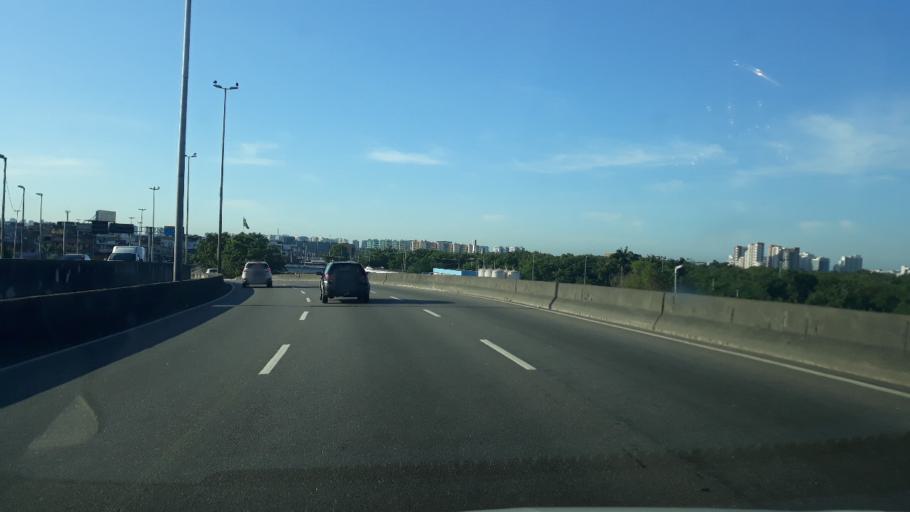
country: BR
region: Rio de Janeiro
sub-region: Sao Joao De Meriti
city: Sao Joao de Meriti
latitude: -22.9543
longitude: -43.3575
